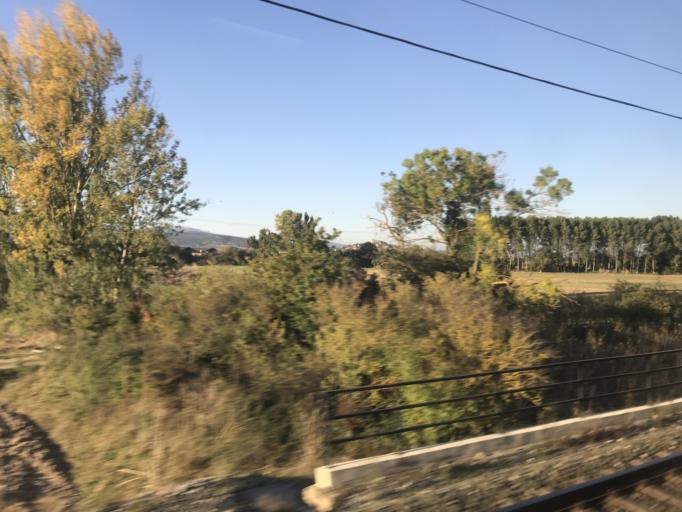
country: ES
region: Basque Country
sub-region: Provincia de Alava
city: Gasteiz / Vitoria
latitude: 42.8508
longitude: -2.7530
